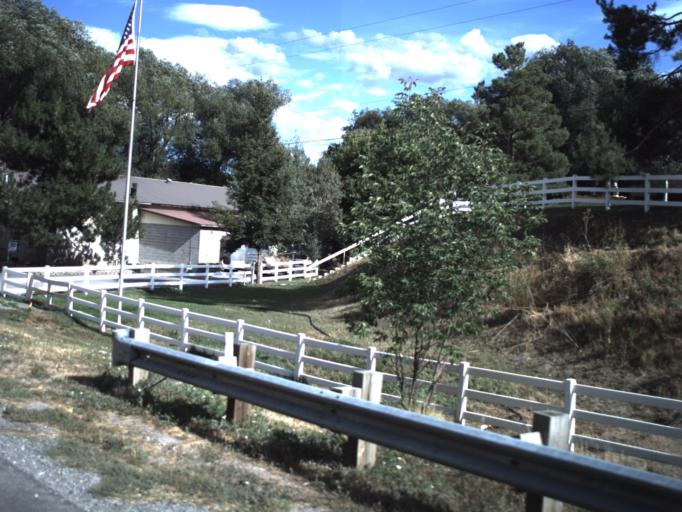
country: US
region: Utah
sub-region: Cache County
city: Wellsville
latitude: 41.6388
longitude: -111.9245
